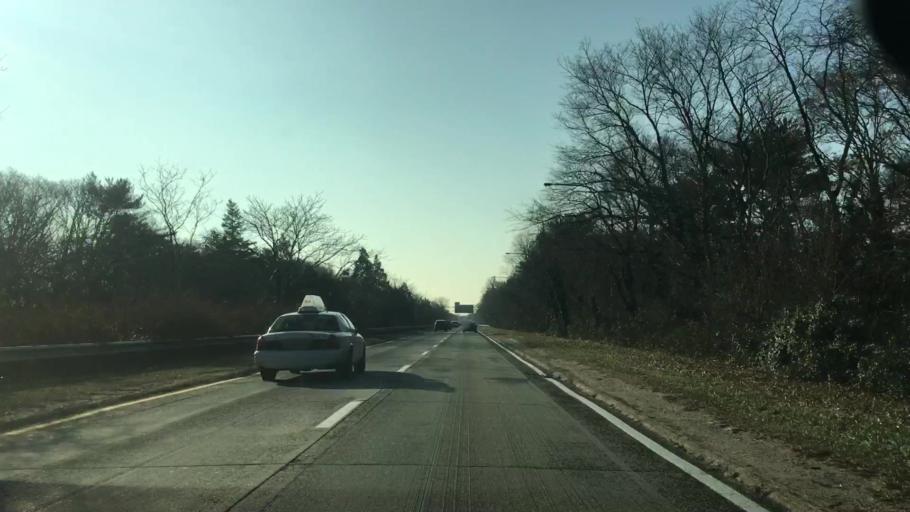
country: US
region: New York
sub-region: Suffolk County
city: Bay Wood
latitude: 40.7591
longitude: -73.2801
